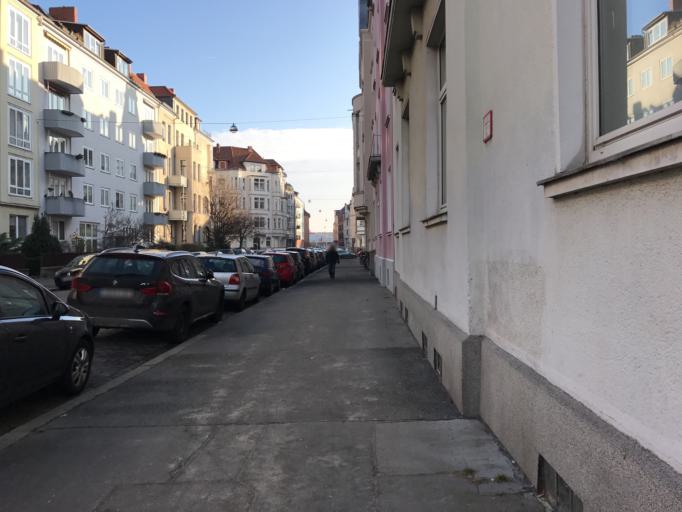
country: DE
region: Lower Saxony
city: Hannover
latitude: 52.3661
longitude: 9.7573
